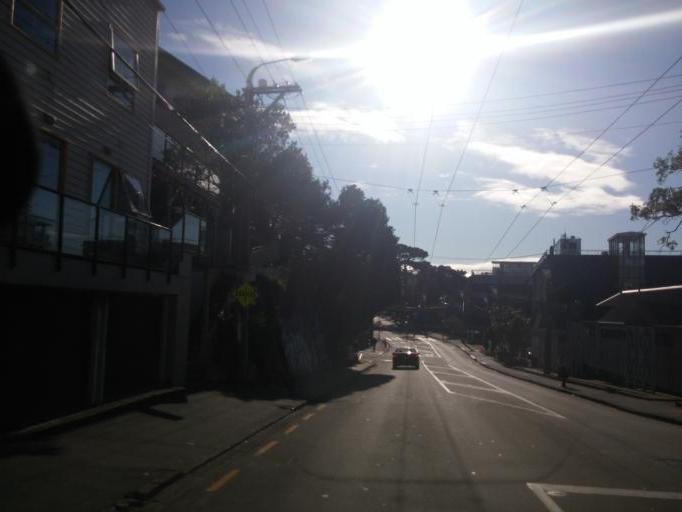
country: NZ
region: Wellington
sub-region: Wellington City
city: Wellington
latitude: -41.3040
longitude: 174.7749
